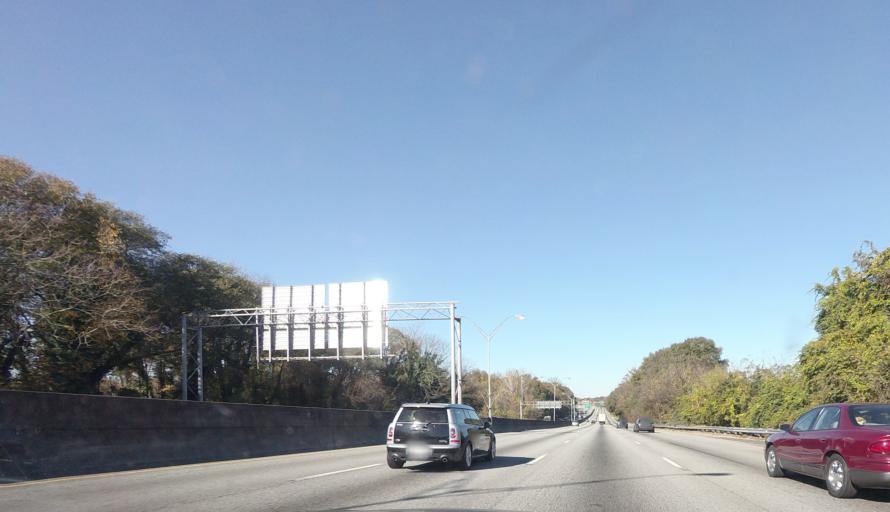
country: US
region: Georgia
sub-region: Fulton County
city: Atlanta
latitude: 33.7426
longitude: -84.4221
